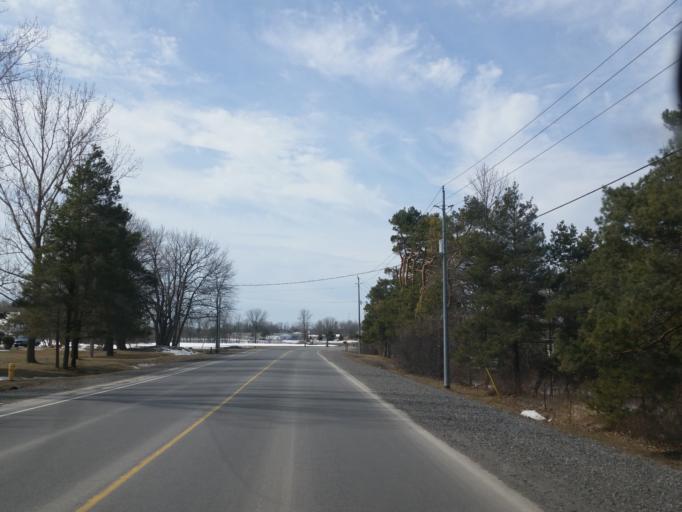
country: CA
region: Ontario
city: Deseronto
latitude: 44.1952
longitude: -77.0697
